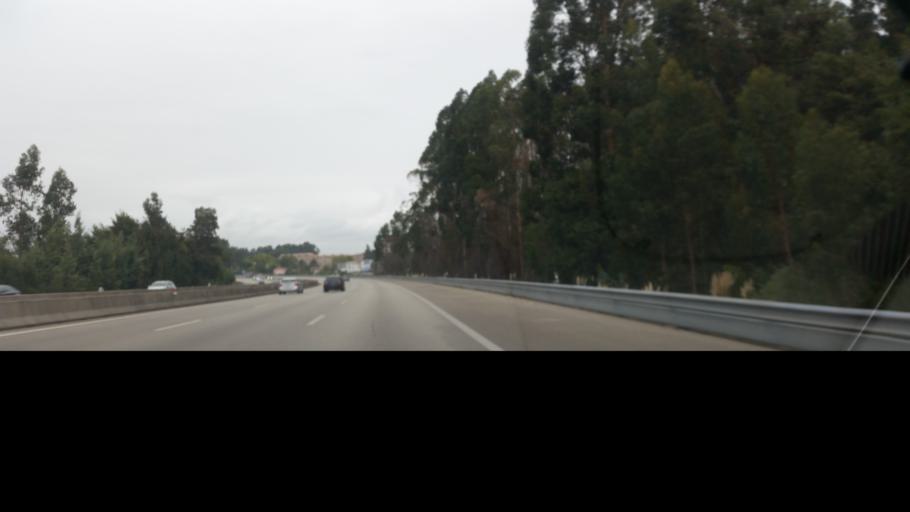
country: PT
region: Porto
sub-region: Trofa
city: Sao Romao do Coronado
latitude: 41.2687
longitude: -8.5609
